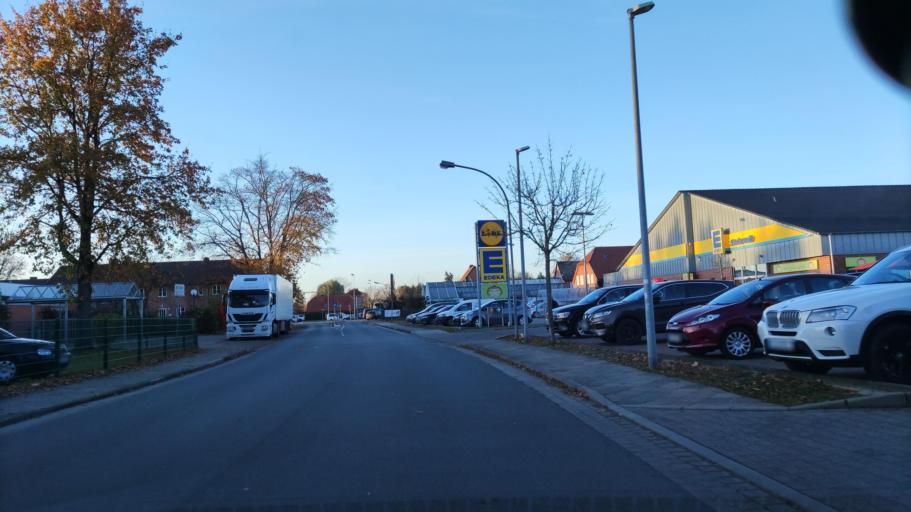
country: DE
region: Lower Saxony
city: Bleckede
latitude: 53.2878
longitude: 10.7307
